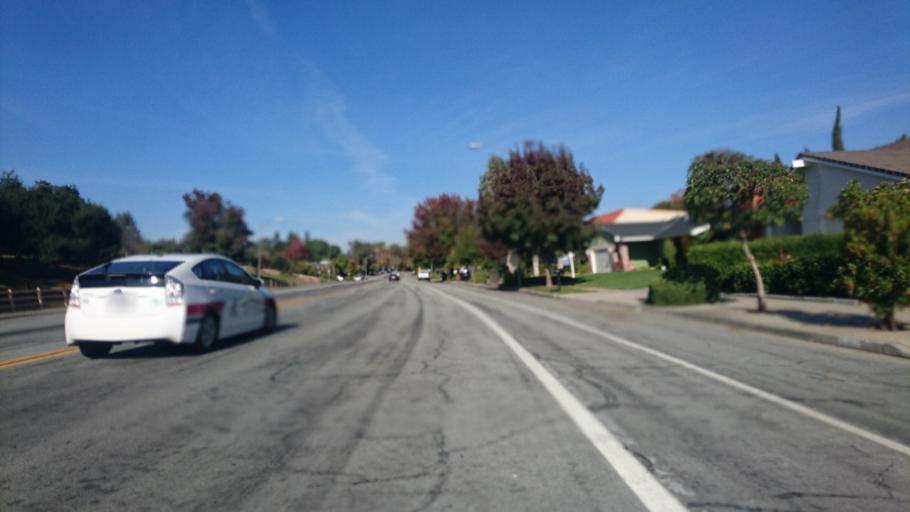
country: US
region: California
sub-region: Santa Clara County
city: Cambrian Park
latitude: 37.2221
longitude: -121.8823
